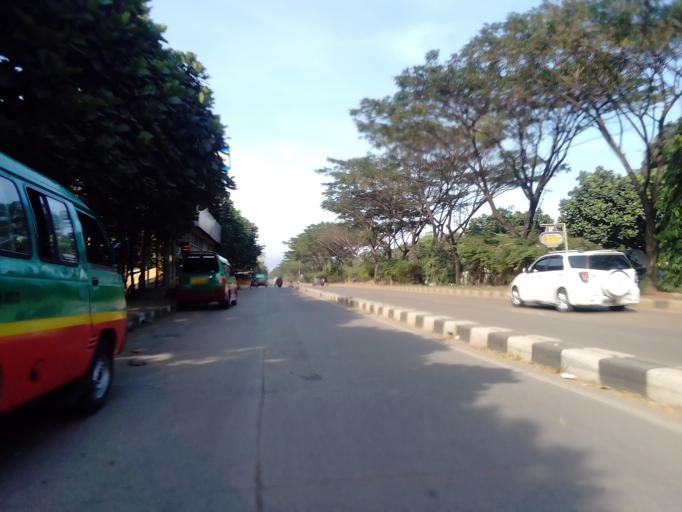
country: ID
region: West Java
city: Cileunyi
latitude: -6.9366
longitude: 107.6973
